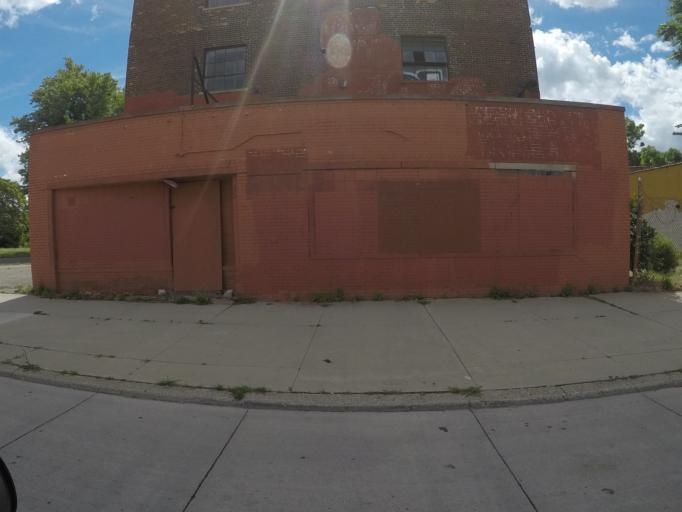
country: US
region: Michigan
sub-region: Wayne County
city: Hamtramck
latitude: 42.3774
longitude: -83.0154
